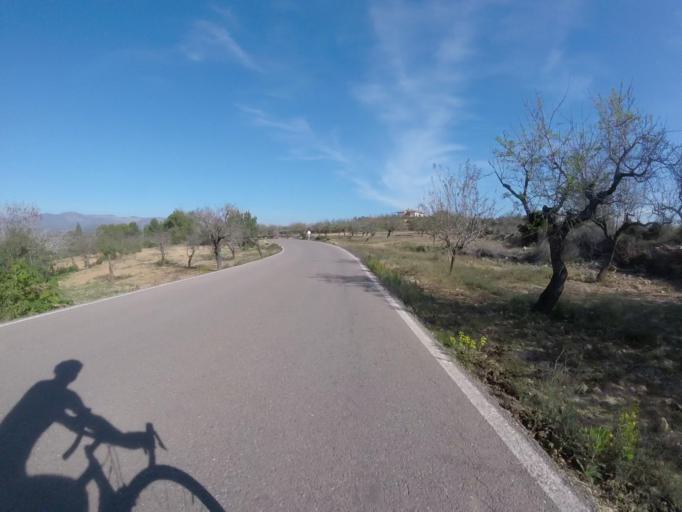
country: ES
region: Valencia
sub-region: Provincia de Castello
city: Benlloch
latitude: 40.2360
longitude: 0.0739
